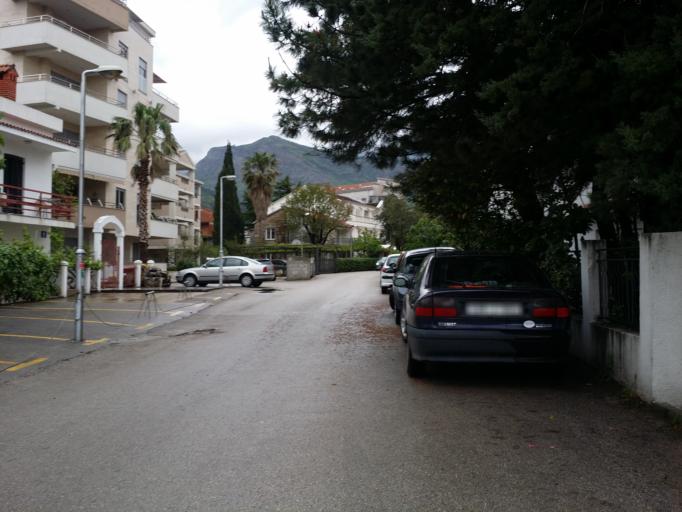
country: ME
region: Budva
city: Budva
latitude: 42.2858
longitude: 18.8399
